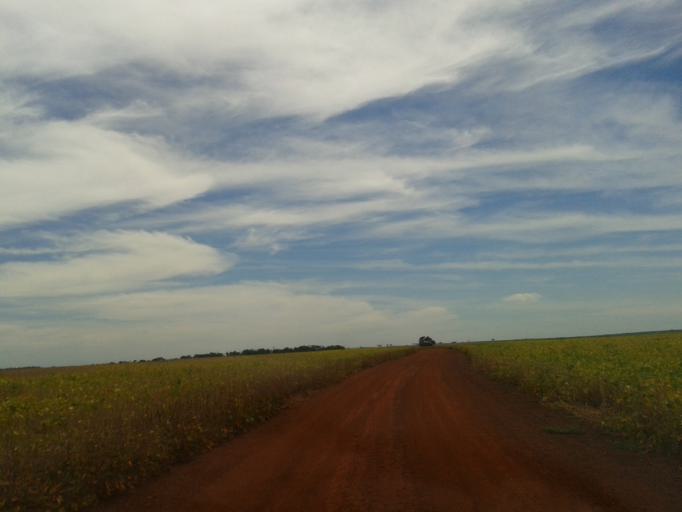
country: BR
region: Minas Gerais
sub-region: Capinopolis
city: Capinopolis
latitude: -18.6814
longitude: -49.7259
